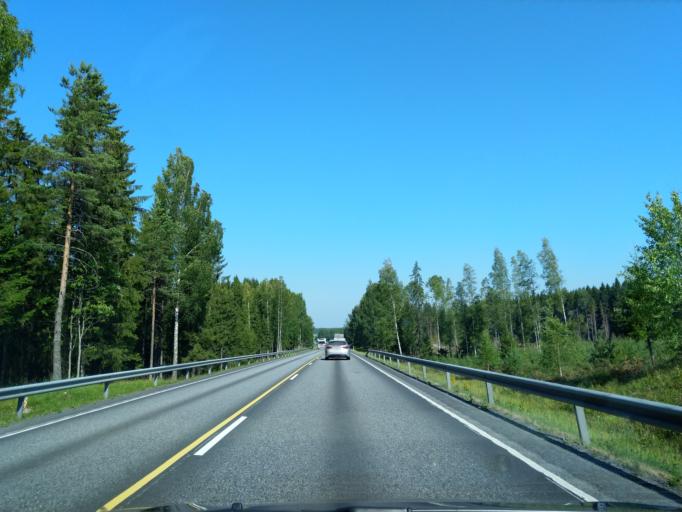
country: FI
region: Varsinais-Suomi
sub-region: Loimaa
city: Alastaro
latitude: 61.0807
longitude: 22.9030
